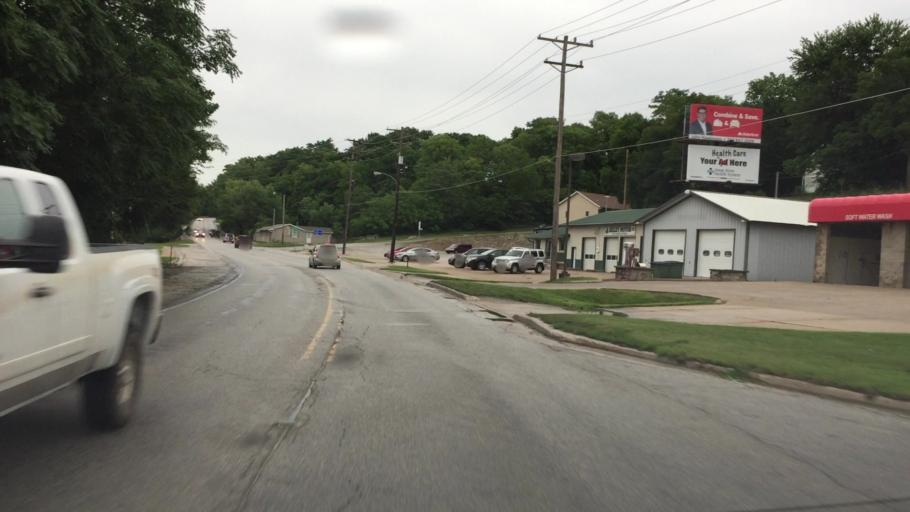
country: US
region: Illinois
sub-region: Hancock County
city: Hamilton
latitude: 40.3919
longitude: -91.3553
